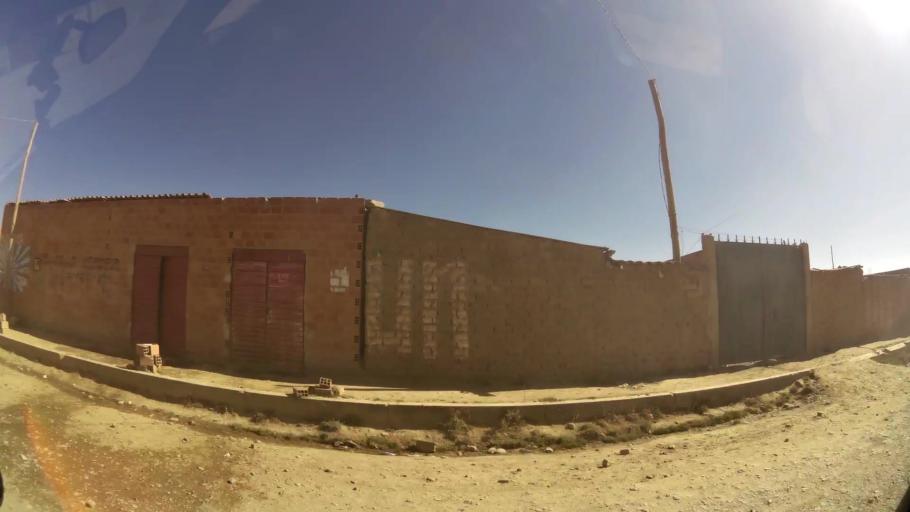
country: BO
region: La Paz
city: La Paz
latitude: -16.6225
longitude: -68.1881
